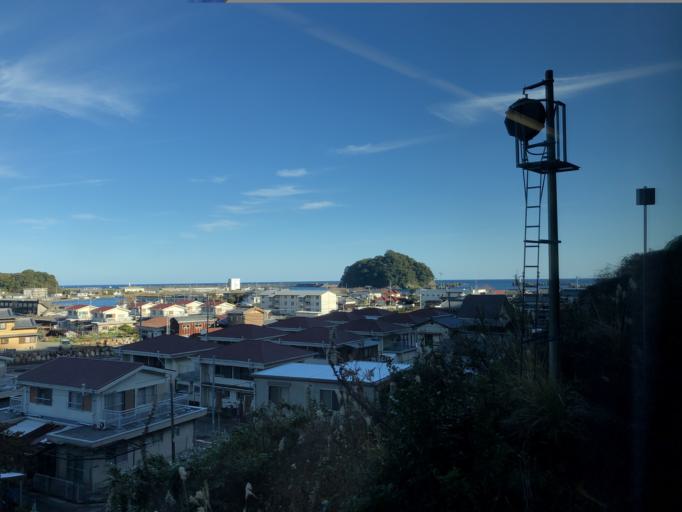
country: JP
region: Kochi
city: Nakamura
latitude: 33.0767
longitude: 133.1037
